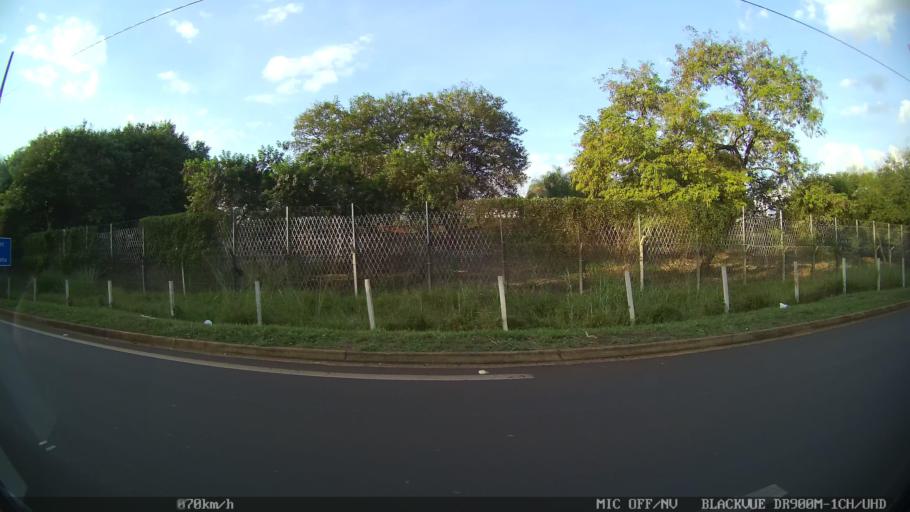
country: BR
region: Sao Paulo
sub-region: Ribeirao Preto
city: Ribeirao Preto
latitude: -21.1085
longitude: -47.8093
